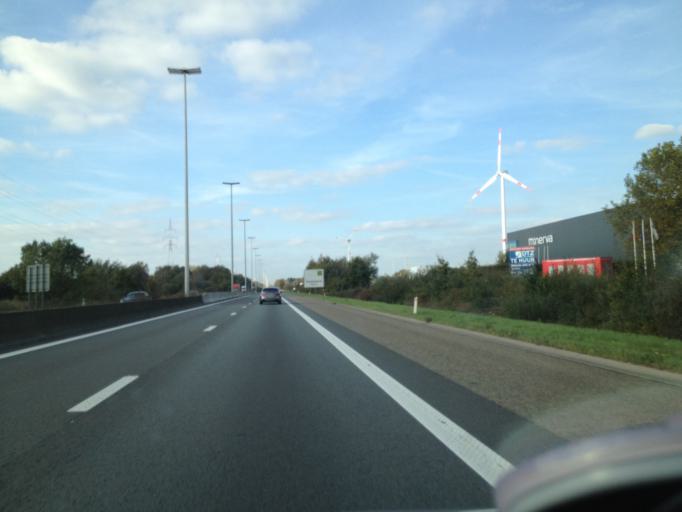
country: BE
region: Flanders
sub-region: Provincie Limburg
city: Beringen
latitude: 51.0537
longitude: 5.1700
